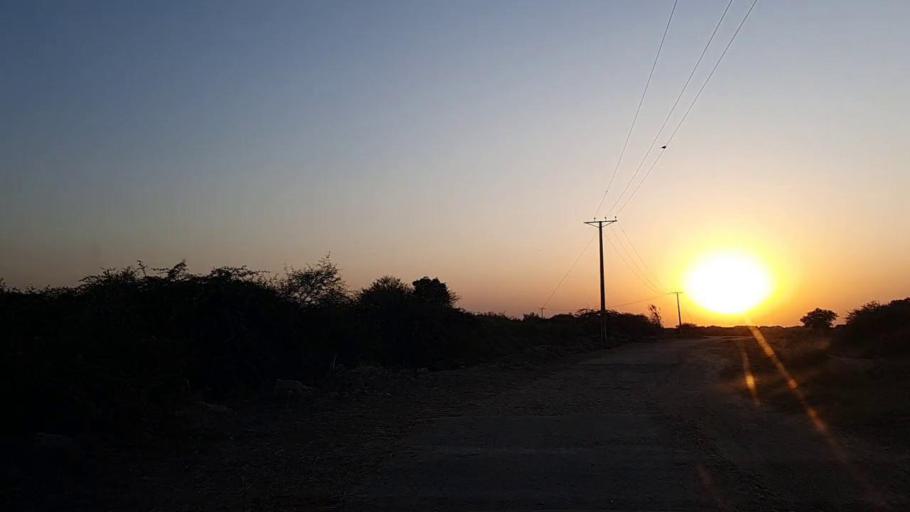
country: PK
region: Sindh
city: Mirpur Batoro
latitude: 24.6325
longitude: 68.1877
